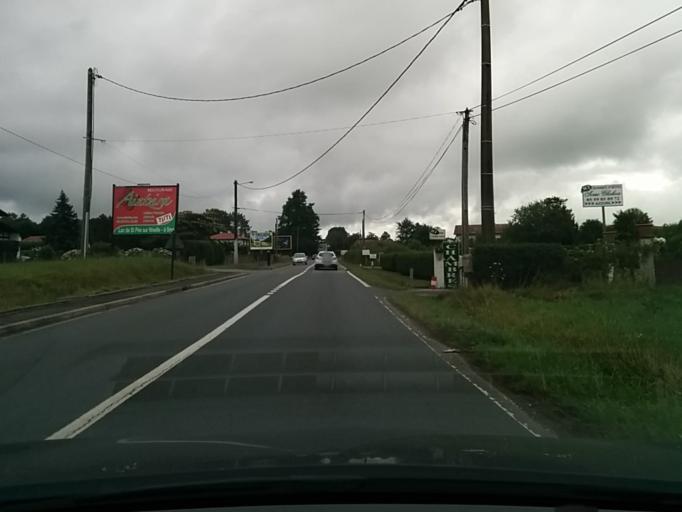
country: FR
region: Aquitaine
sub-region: Departement des Pyrenees-Atlantiques
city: Saint-Pee-sur-Nivelle
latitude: 43.3576
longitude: -1.5740
